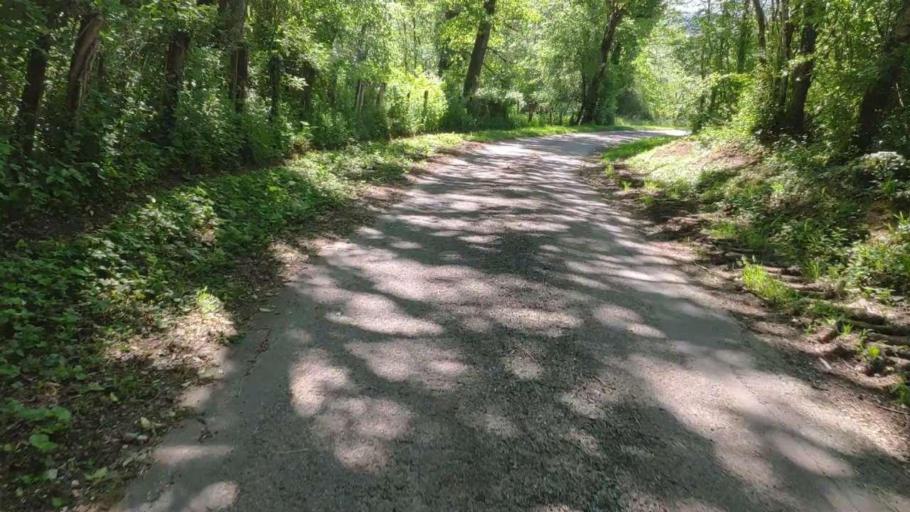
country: FR
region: Franche-Comte
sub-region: Departement du Jura
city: Clairvaux-les-Lacs
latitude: 46.7085
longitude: 5.7627
